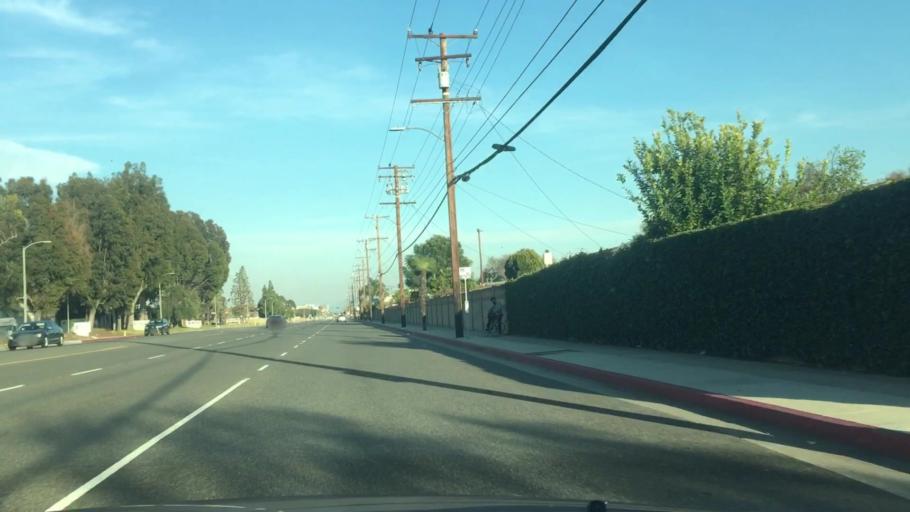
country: US
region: California
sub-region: Orange County
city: La Palma
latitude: 33.8587
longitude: -118.0236
